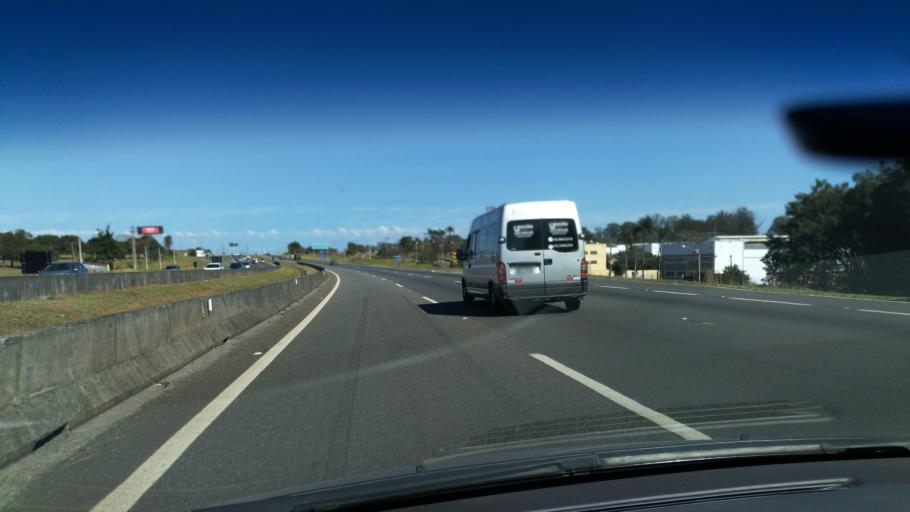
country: BR
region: Sao Paulo
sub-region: Jaguariuna
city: Jaguariuna
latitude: -22.7907
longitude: -47.0317
